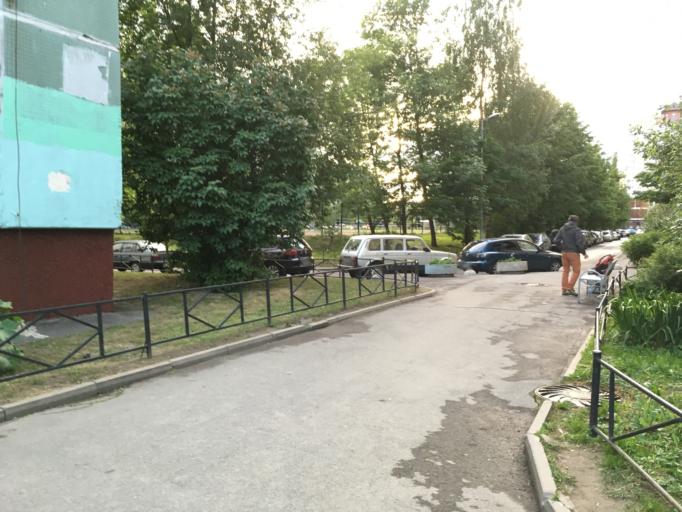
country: RU
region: St.-Petersburg
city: Staraya Derevnya
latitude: 60.0153
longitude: 30.2392
